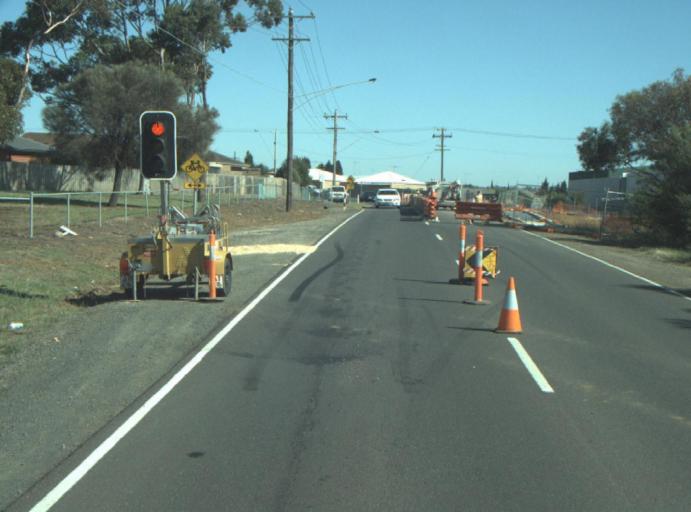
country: AU
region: Victoria
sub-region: Greater Geelong
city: Bell Park
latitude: -38.1006
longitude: 144.3423
